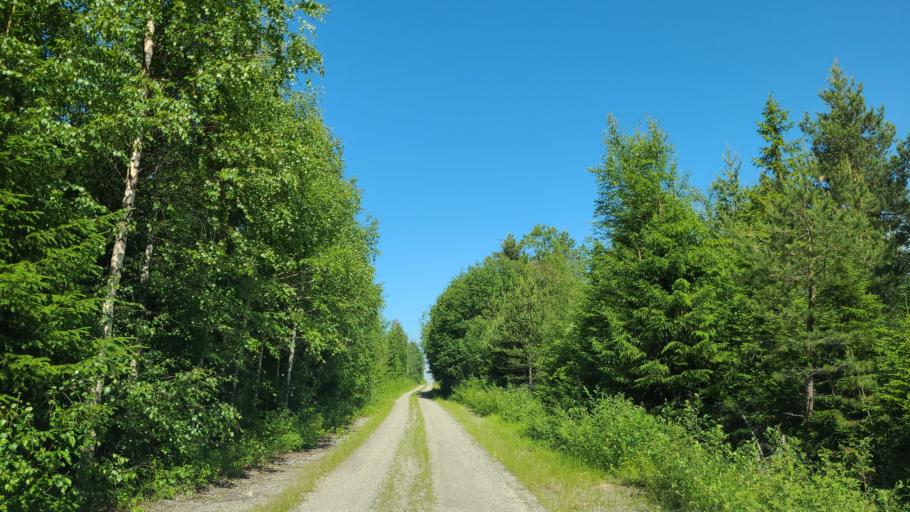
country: SE
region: Vaesternorrland
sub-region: OErnskoeldsviks Kommun
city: Husum
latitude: 63.4349
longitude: 19.2307
